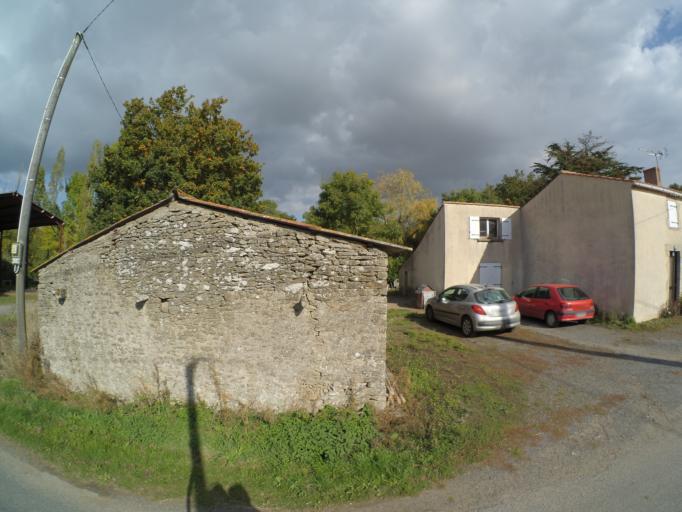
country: FR
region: Pays de la Loire
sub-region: Departement de la Loire-Atlantique
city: Remouille
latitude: 47.0696
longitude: -1.3579
